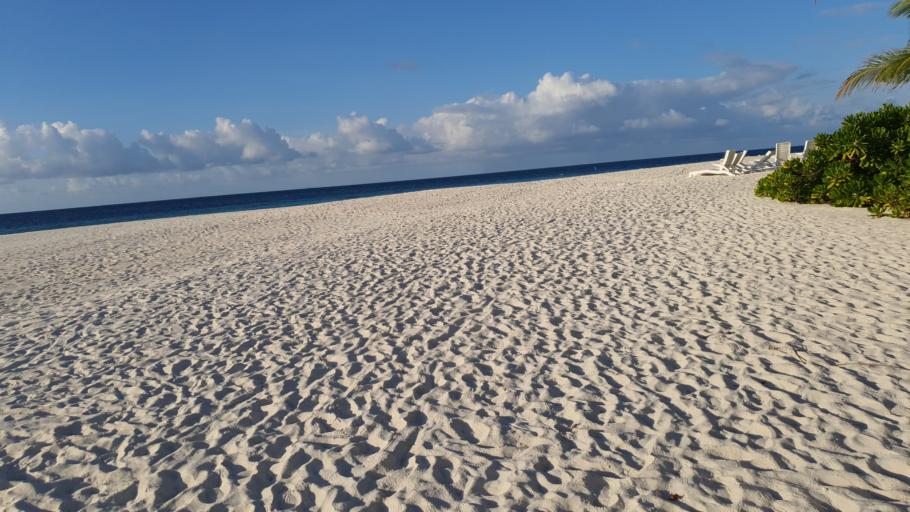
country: MV
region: North Central
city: Mahibadhoo
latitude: 3.6517
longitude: 72.8228
